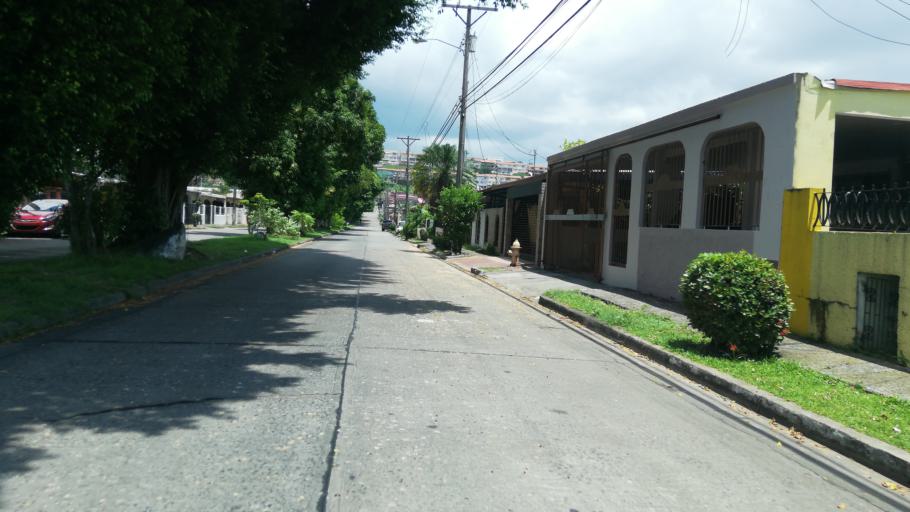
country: PA
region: Panama
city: San Miguelito
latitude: 9.0578
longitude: -79.4563
